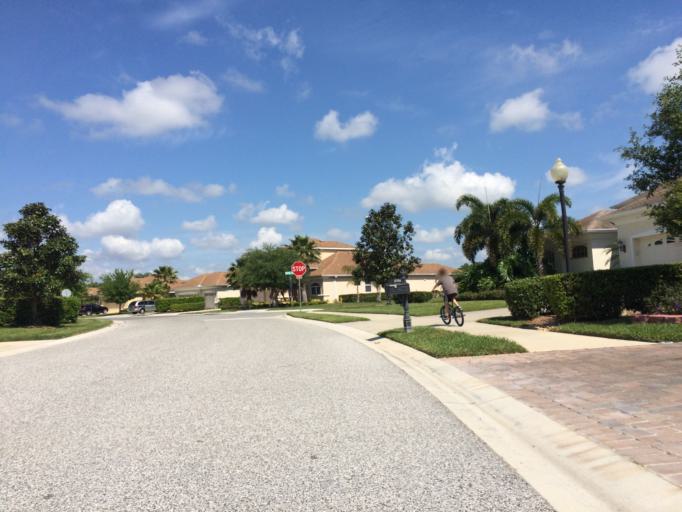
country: US
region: Florida
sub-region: Manatee County
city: Ellenton
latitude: 27.5046
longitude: -82.4223
